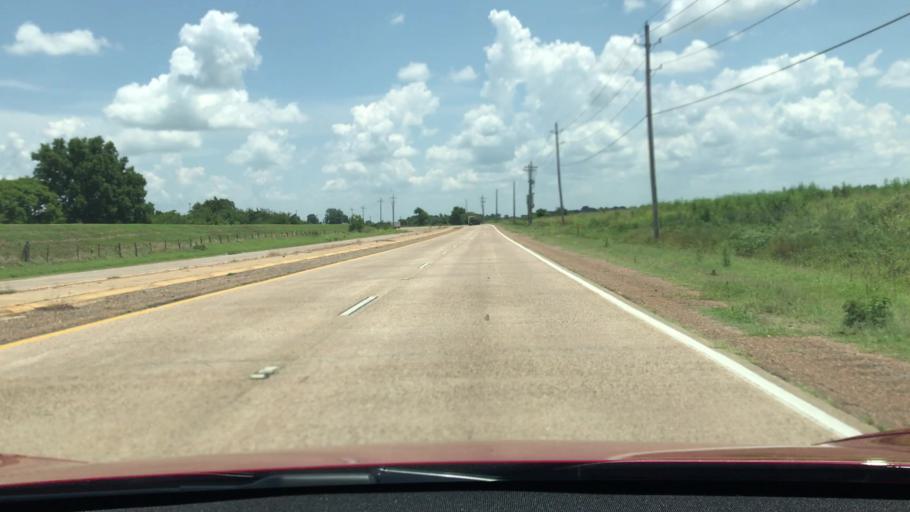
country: US
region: Louisiana
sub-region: Bossier Parish
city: Bossier City
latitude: 32.3922
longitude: -93.6856
